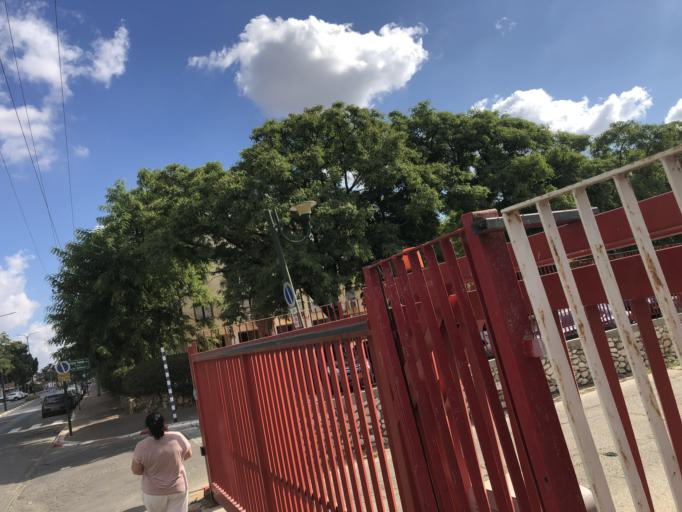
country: IL
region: Central District
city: Yehud
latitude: 32.0292
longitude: 34.8972
